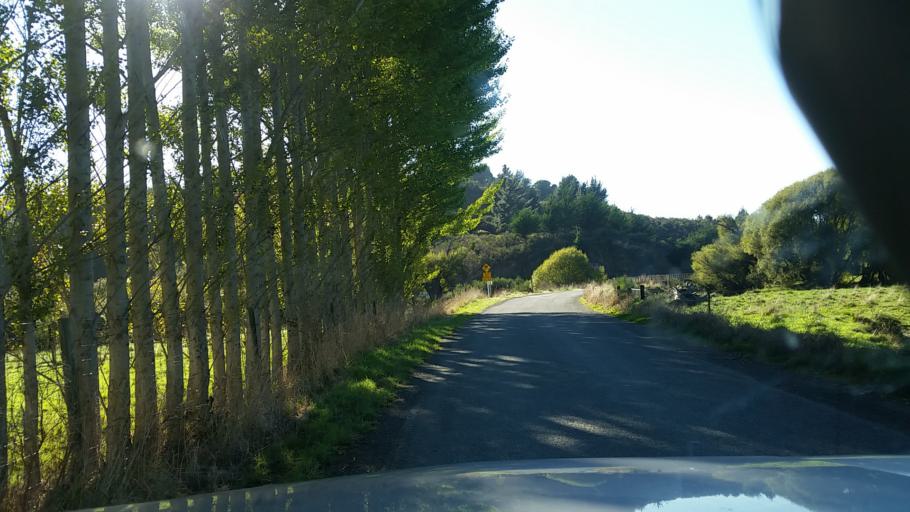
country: NZ
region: Marlborough
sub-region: Marlborough District
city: Blenheim
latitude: -41.4406
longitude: 173.8997
